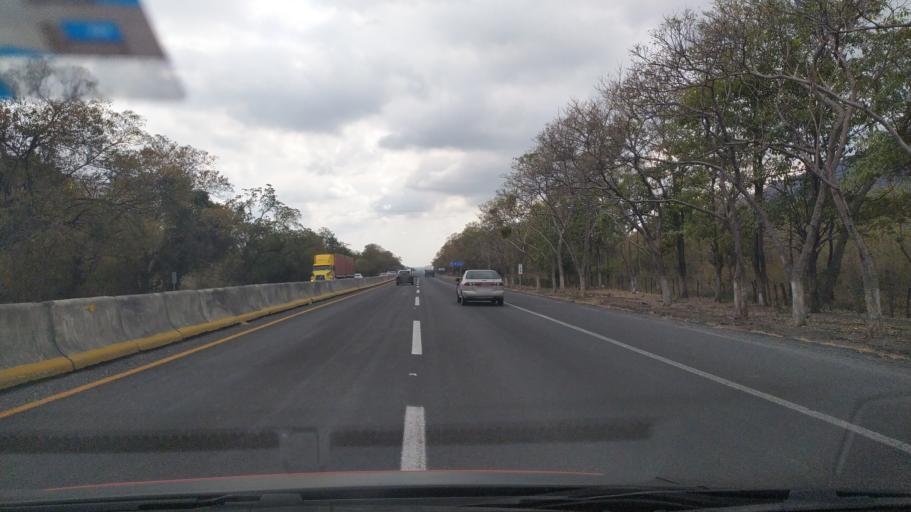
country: MX
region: Colima
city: Madrid
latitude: 19.0113
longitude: -103.8319
